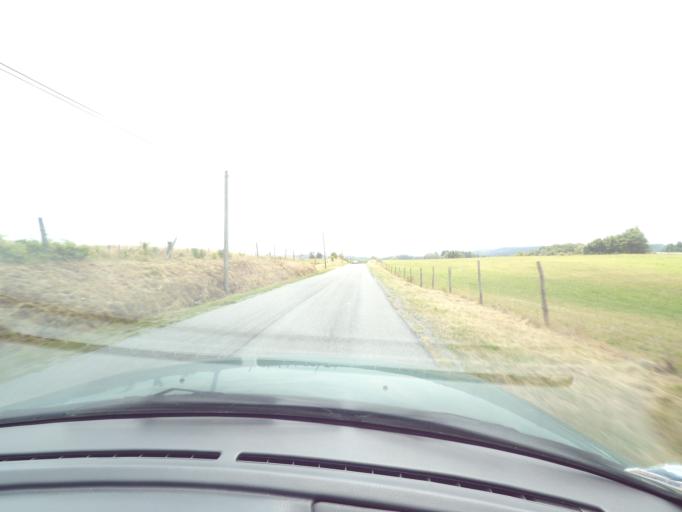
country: FR
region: Limousin
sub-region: Departement de la Correze
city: Bugeat
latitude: 45.7114
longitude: 2.0173
